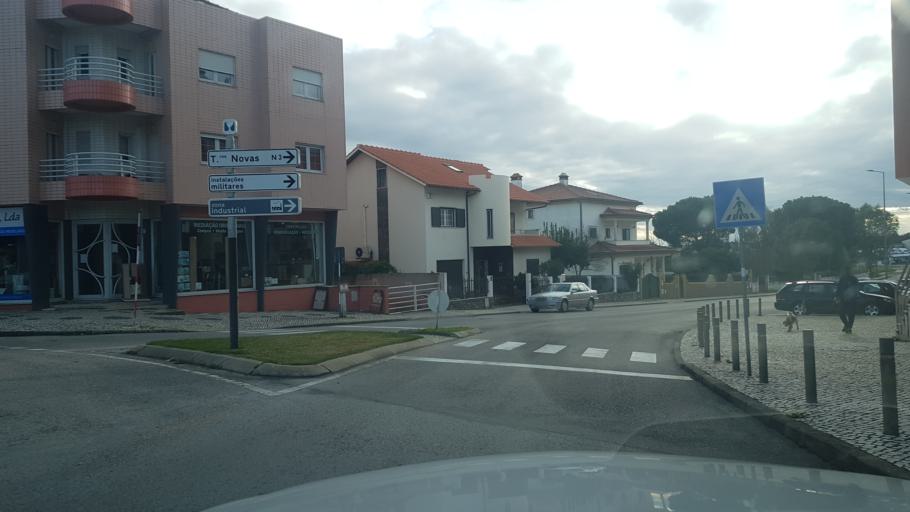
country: PT
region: Santarem
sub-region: Entroncamento
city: Entroncamento
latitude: 39.4705
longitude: -8.4835
